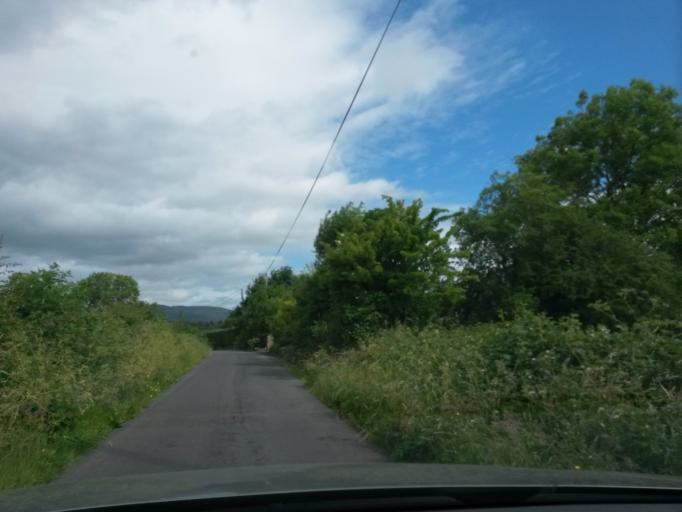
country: IE
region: Connaught
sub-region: County Leitrim
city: Manorhamilton
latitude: 54.2293
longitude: -8.3123
